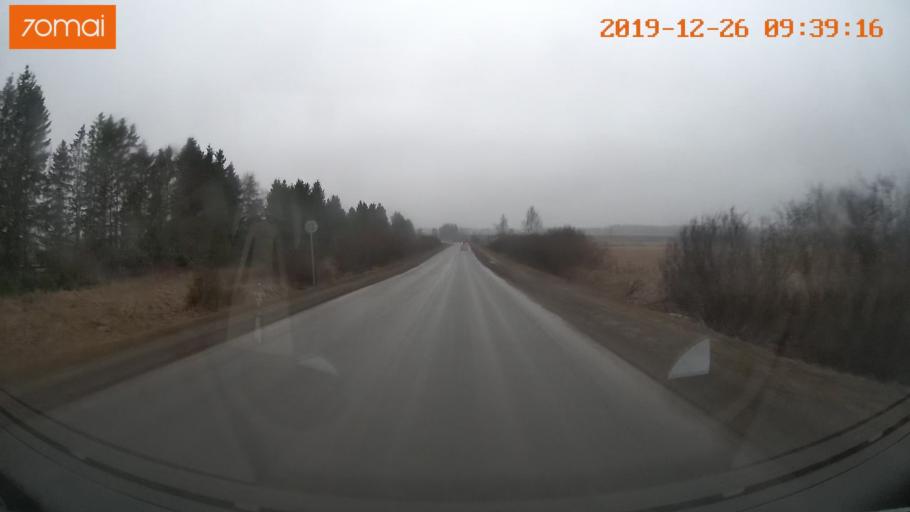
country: RU
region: Vologda
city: Vologda
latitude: 59.1528
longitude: 40.0282
